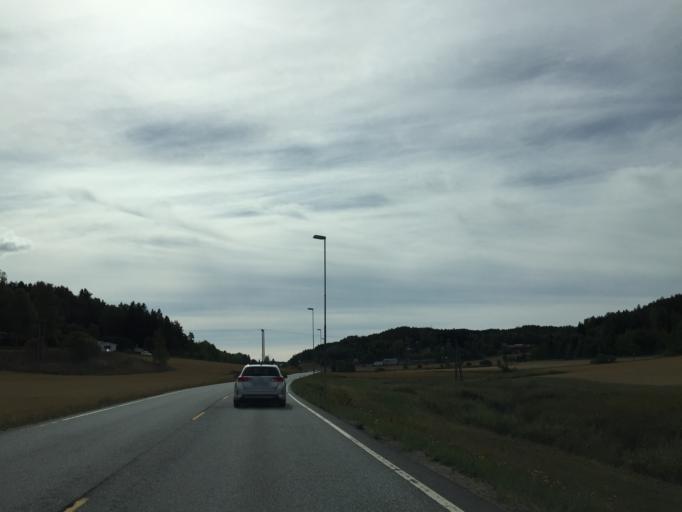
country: NO
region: Ostfold
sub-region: Fredrikstad
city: Fredrikstad
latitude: 59.2558
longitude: 10.8944
